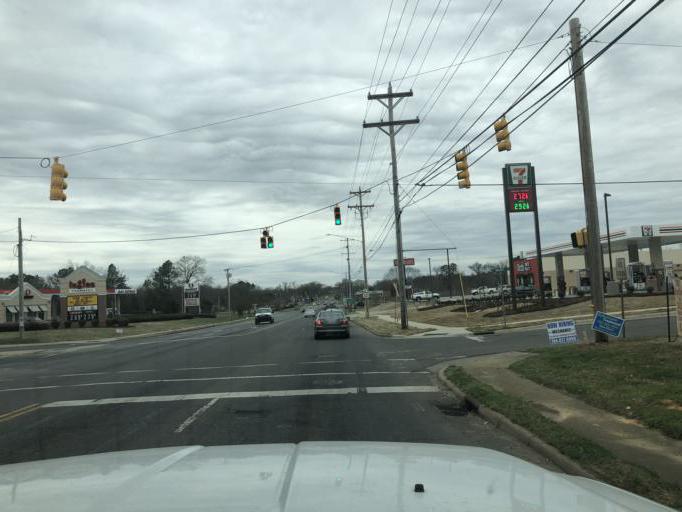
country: US
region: North Carolina
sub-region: Gaston County
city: Dallas
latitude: 35.3166
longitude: -81.1840
